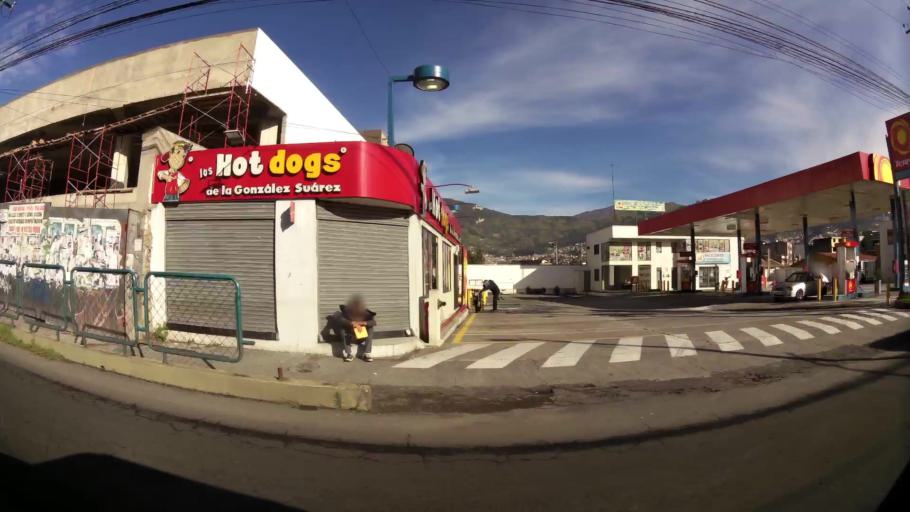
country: EC
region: Pichincha
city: Quito
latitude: -0.2498
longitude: -78.5210
